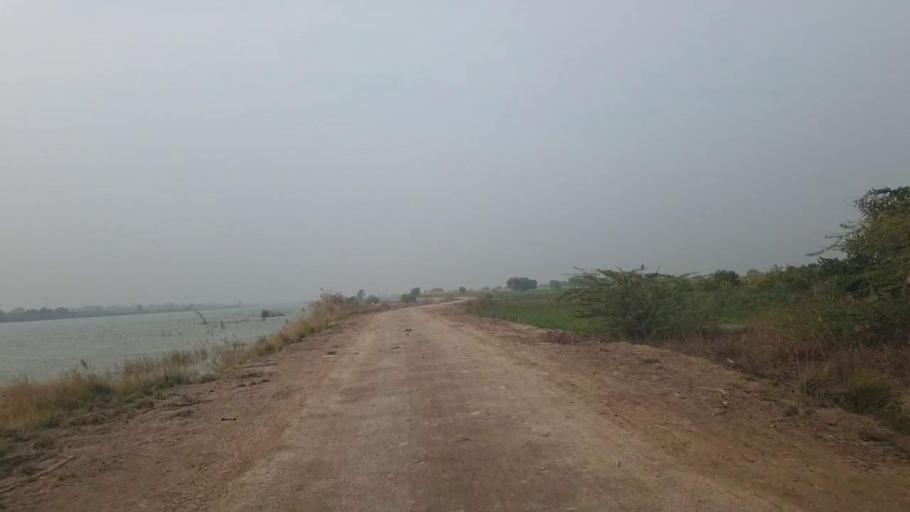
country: PK
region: Sindh
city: Berani
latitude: 25.8155
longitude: 68.7385
